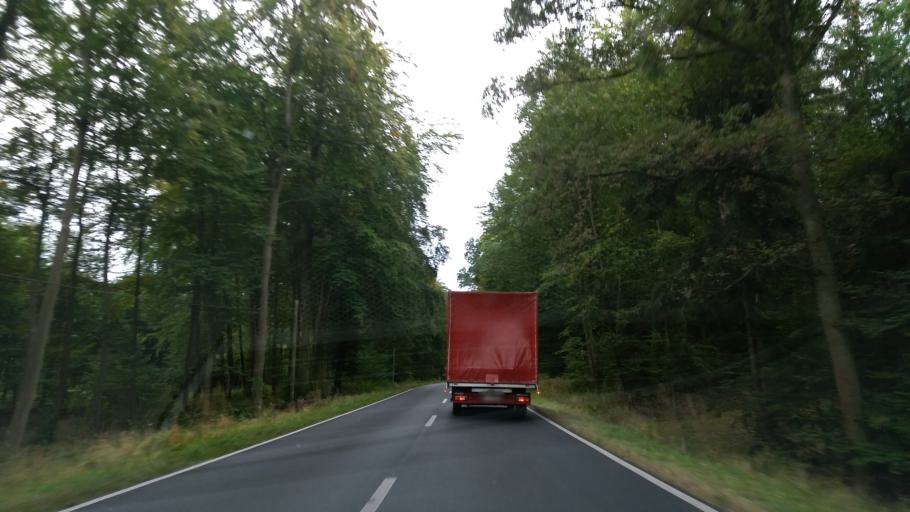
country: PL
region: West Pomeranian Voivodeship
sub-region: Powiat mysliborski
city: Barlinek
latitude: 52.9387
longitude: 15.1914
